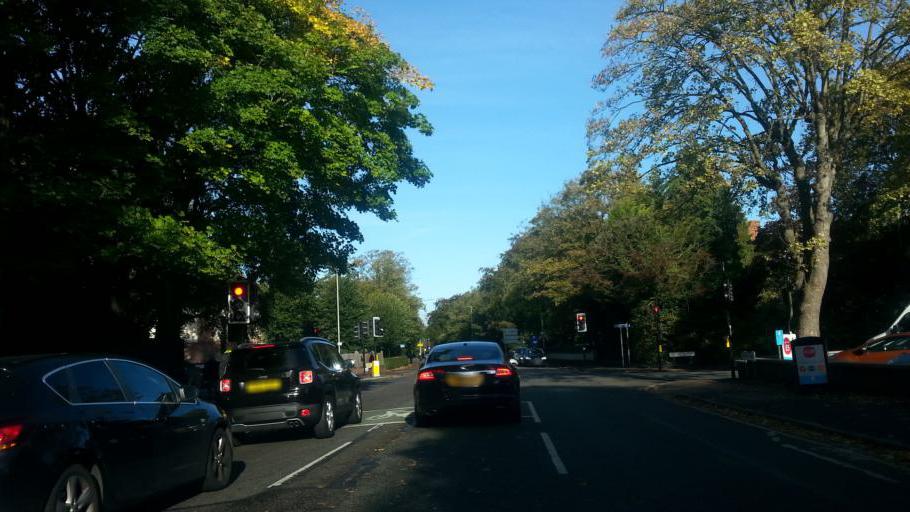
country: GB
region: England
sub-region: Leicestershire
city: Oadby
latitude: 52.6140
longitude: -1.1038
